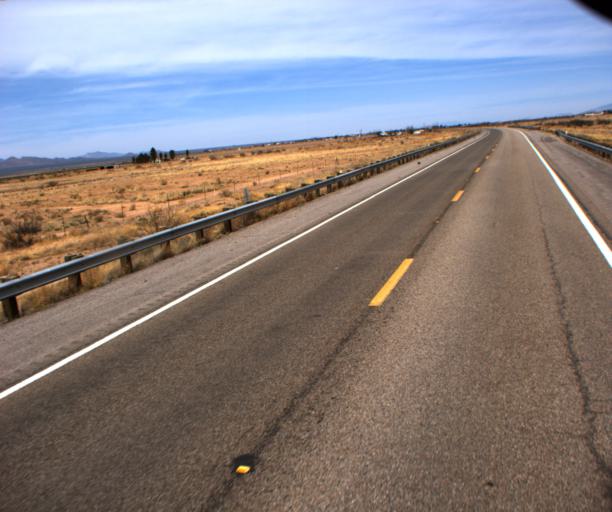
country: US
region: Arizona
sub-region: Cochise County
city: Pirtleville
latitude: 31.6442
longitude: -109.6727
